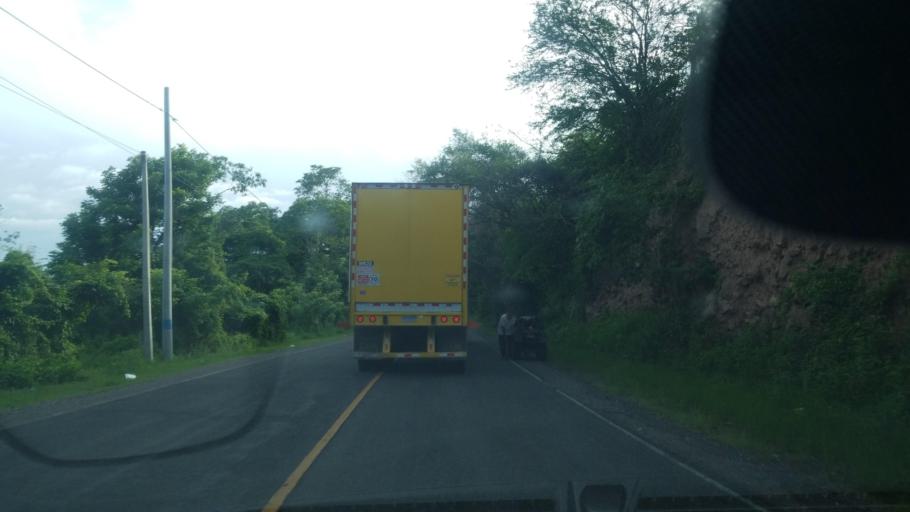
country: HN
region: Santa Barbara
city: Ilama
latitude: 15.0689
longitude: -88.2280
